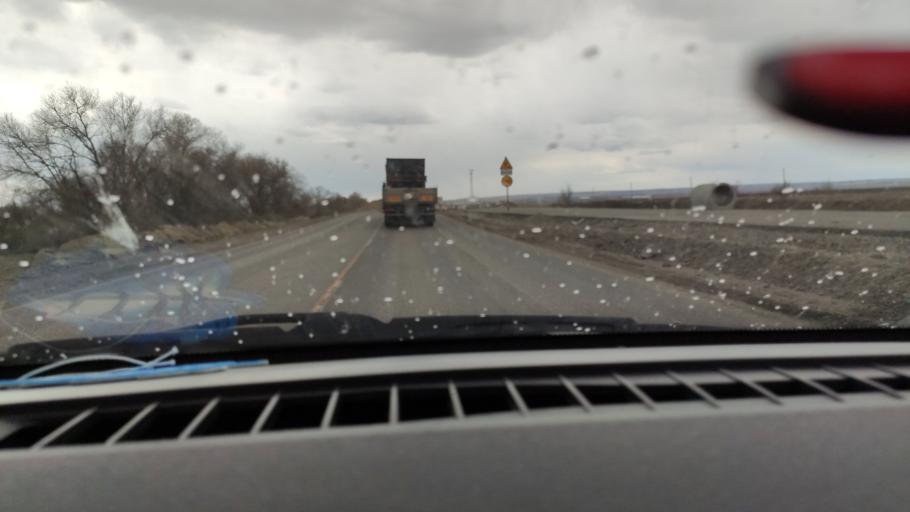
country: RU
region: Saratov
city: Sinodskoye
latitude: 52.0029
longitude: 46.6805
